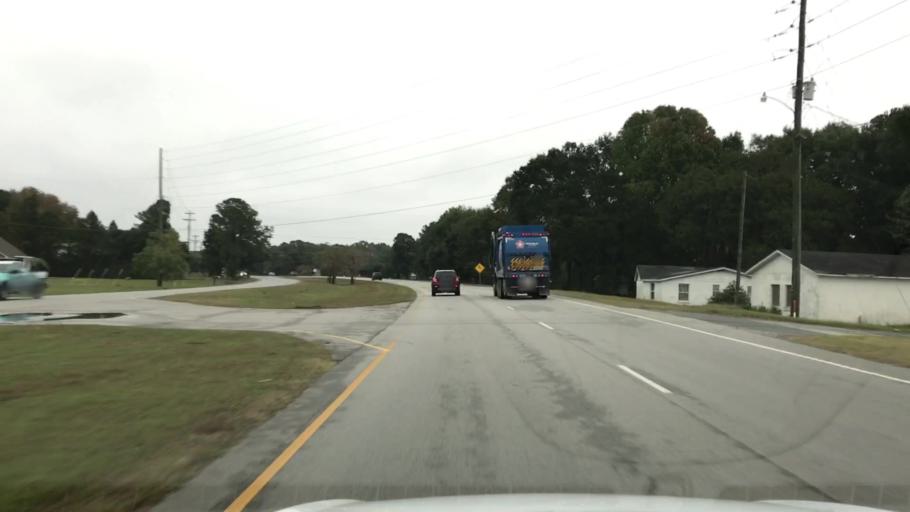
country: US
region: South Carolina
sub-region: Charleston County
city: Isle of Palms
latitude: 32.8837
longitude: -79.7516
